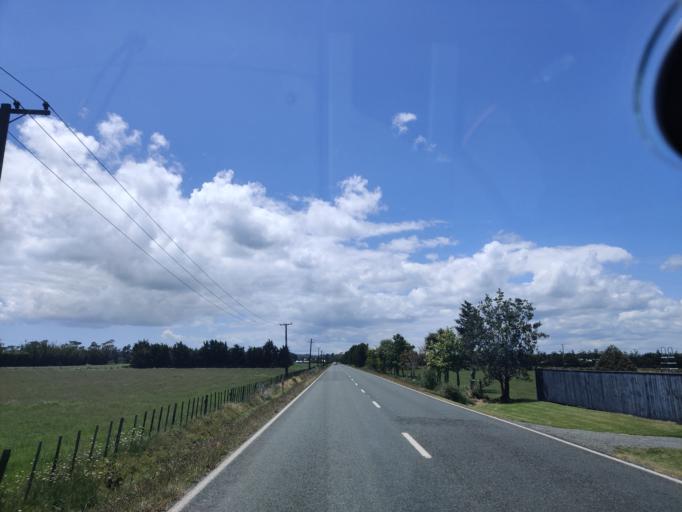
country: NZ
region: Northland
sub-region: Far North District
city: Kaitaia
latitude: -35.0253
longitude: 173.2394
